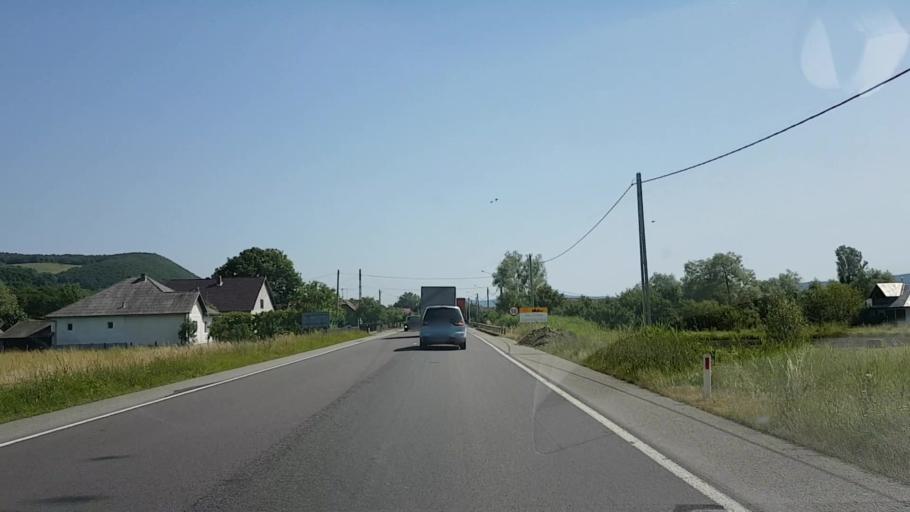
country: RO
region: Bistrita-Nasaud
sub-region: Comuna Sieu-Odorhei
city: Sieu-Odorhei
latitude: 47.1558
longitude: 24.3062
